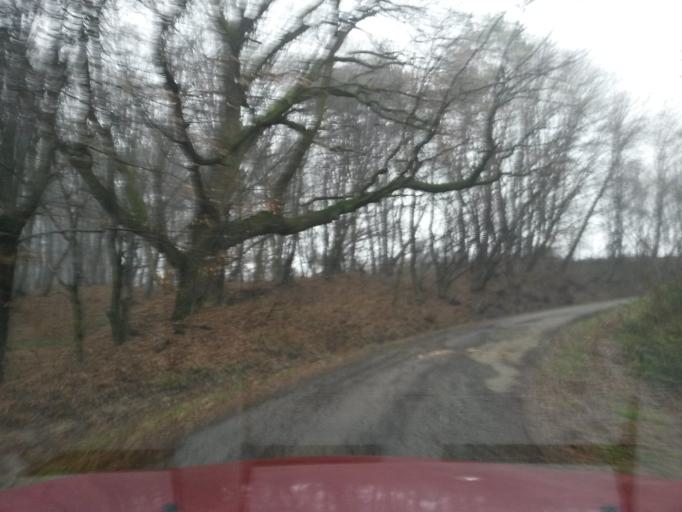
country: SK
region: Presovsky
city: Vranov nad Topl'ou
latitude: 48.8865
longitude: 21.7550
